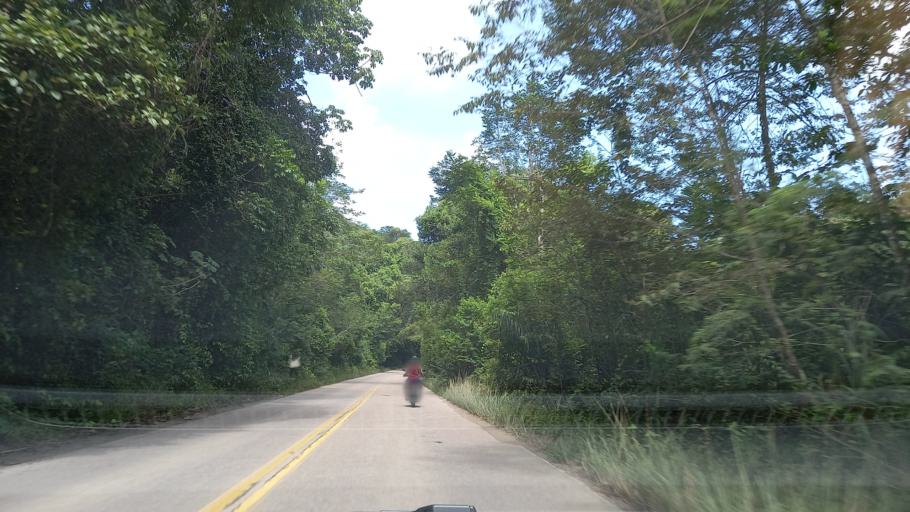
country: BR
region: Pernambuco
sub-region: Rio Formoso
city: Rio Formoso
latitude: -8.7347
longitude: -35.1734
